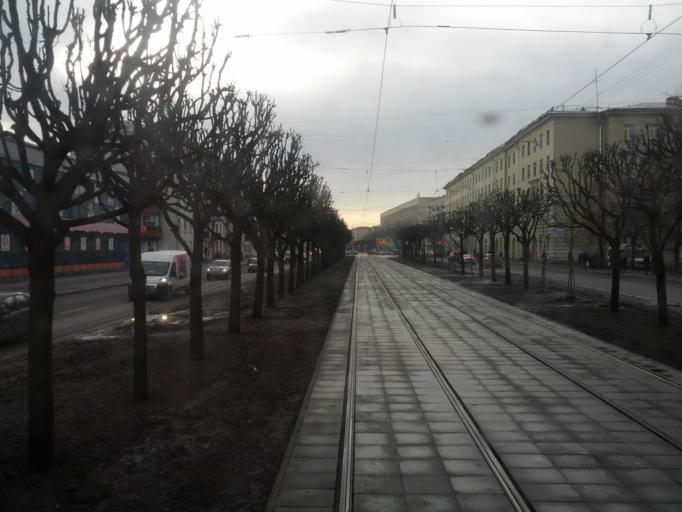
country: RU
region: St.-Petersburg
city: Centralniy
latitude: 59.9264
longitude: 30.4144
